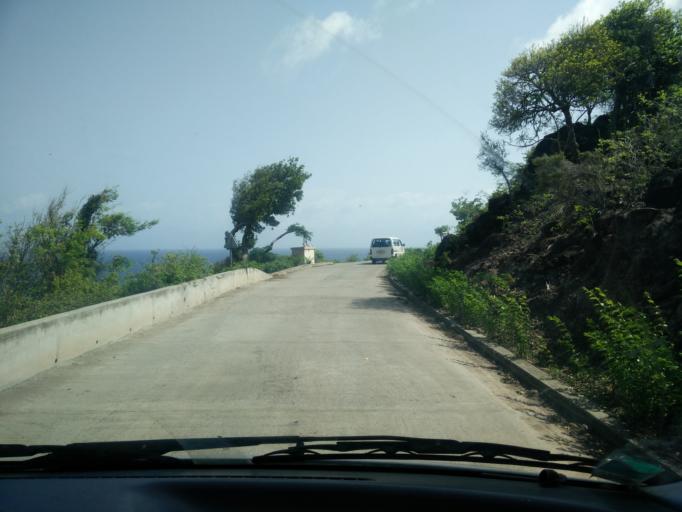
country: GP
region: Guadeloupe
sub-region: Guadeloupe
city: Terre-de-Bas
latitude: 15.8455
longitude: -61.6274
